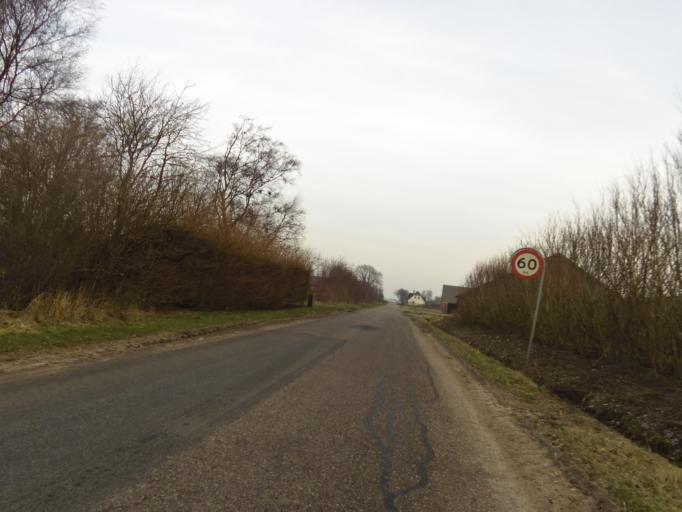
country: DK
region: South Denmark
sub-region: Haderslev Kommune
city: Gram
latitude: 55.3484
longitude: 8.9375
